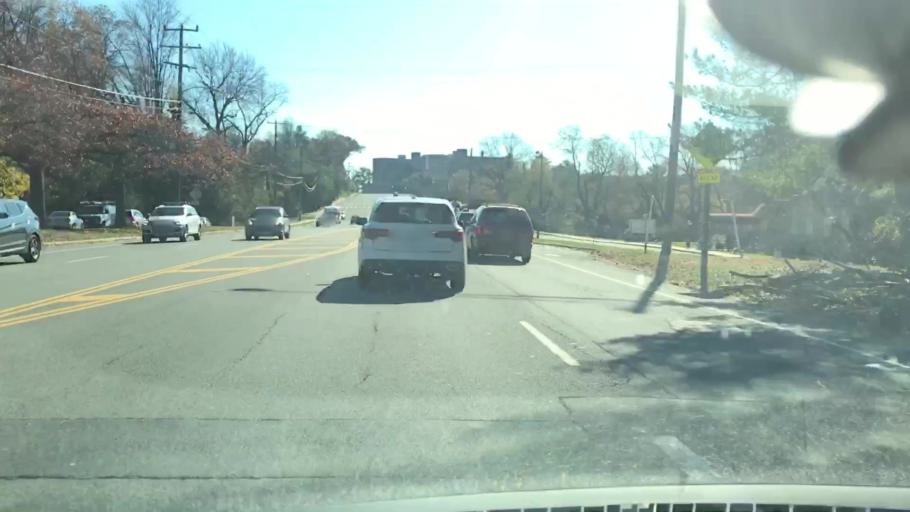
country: US
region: Virginia
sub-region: Fairfax County
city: Seven Corners
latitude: 38.8631
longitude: -77.1488
